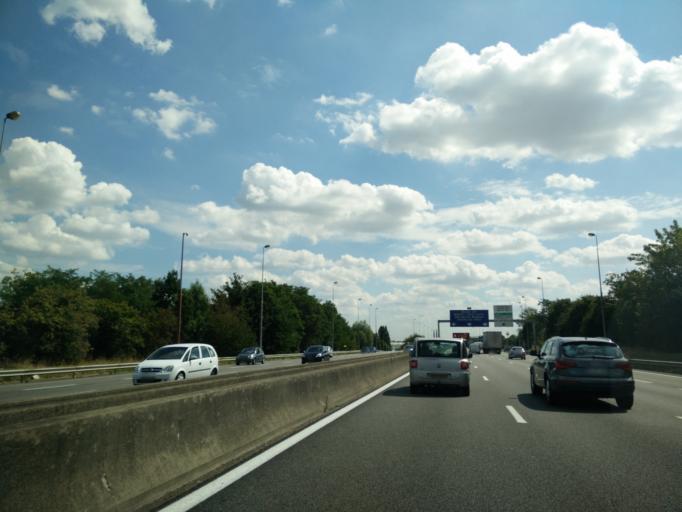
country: FR
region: Ile-de-France
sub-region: Departement des Yvelines
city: Mantes-la-Ville
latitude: 48.9818
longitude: 1.6904
